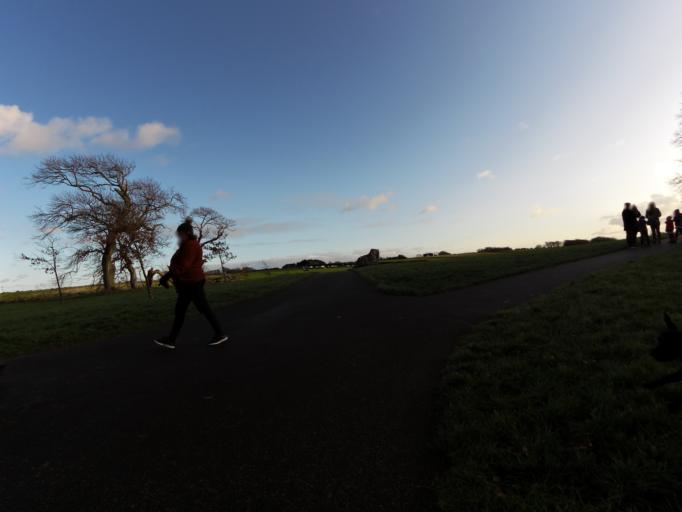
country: IE
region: Connaught
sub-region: County Galway
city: Oranmore
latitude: 53.2473
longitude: -8.9623
